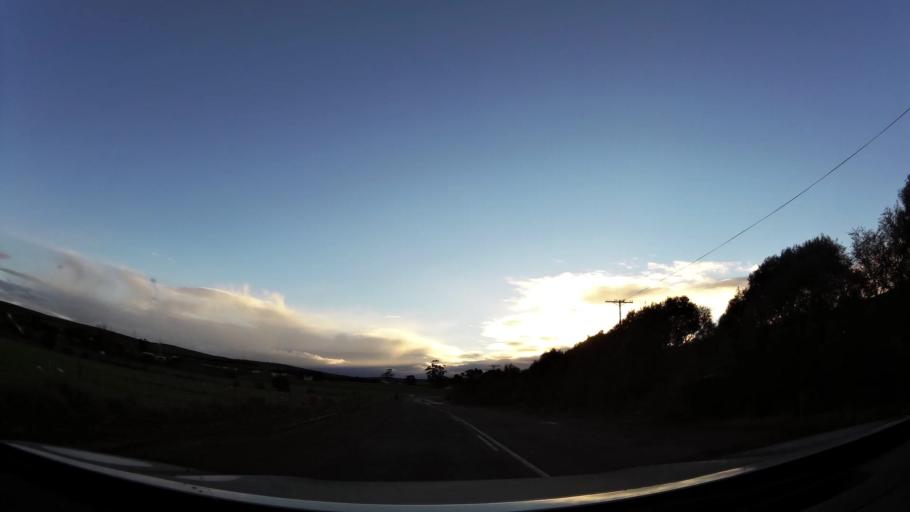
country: ZA
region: Western Cape
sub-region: Eden District Municipality
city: Riversdale
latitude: -34.0789
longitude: 20.9266
